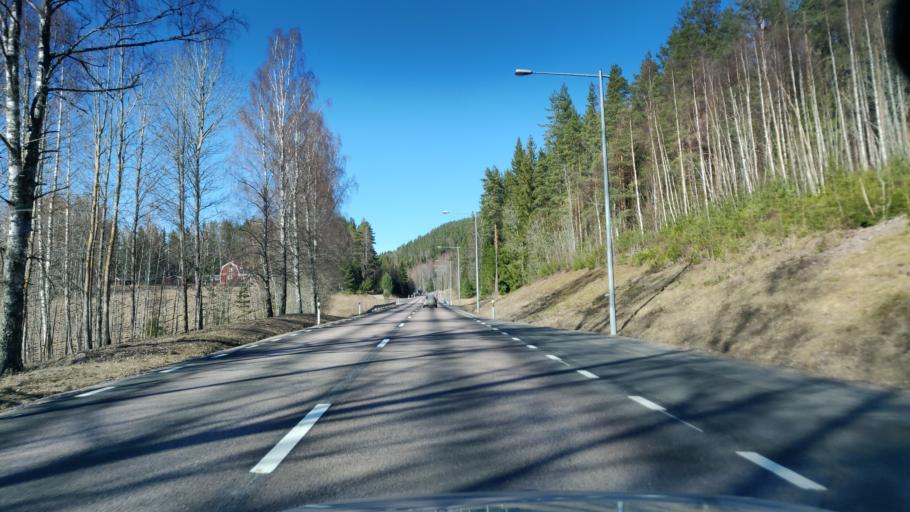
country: SE
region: Vaermland
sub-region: Hagfors Kommun
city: Hagfors
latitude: 59.9342
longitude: 13.6765
